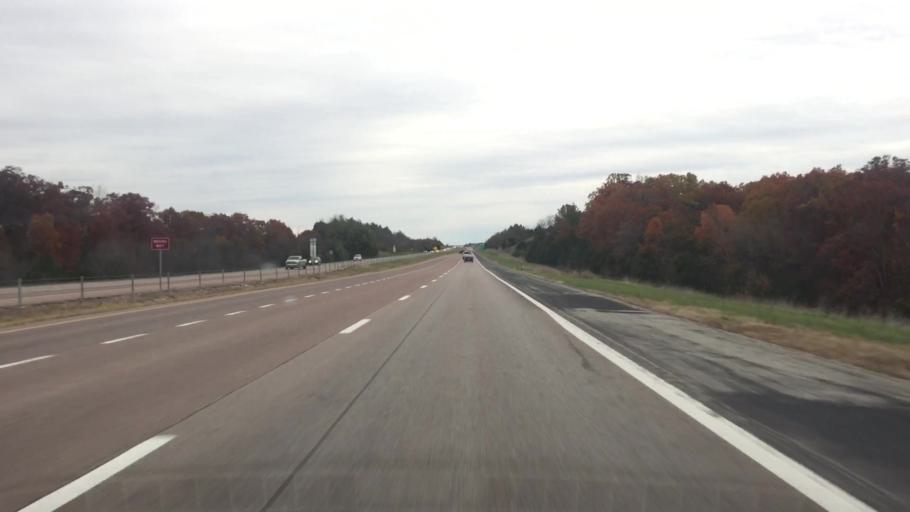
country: US
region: Missouri
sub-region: Boone County
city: Ashland
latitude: 38.7504
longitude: -92.2531
